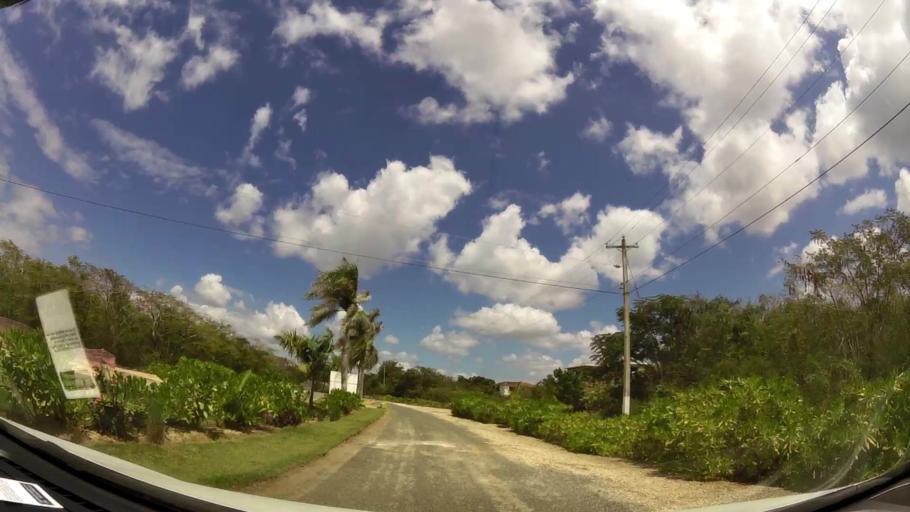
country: DO
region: Santo Domingo
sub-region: Santo Domingo
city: Boca Chica
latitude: 18.4644
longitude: -69.6542
